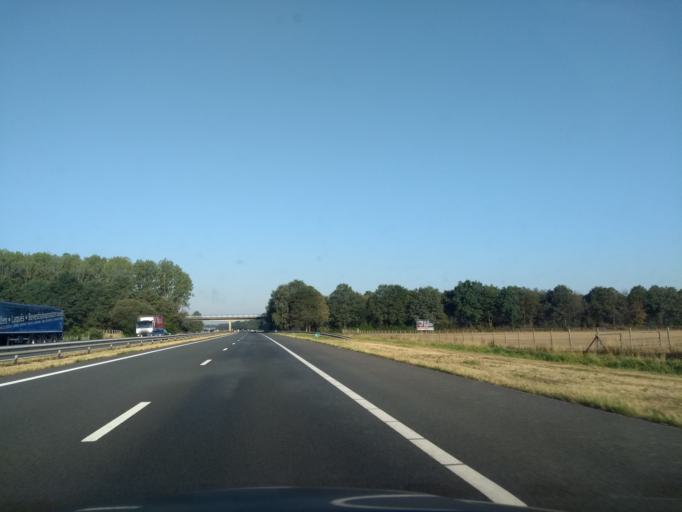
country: NL
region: Gelderland
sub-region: Oude IJsselstreek
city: Wisch
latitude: 51.9445
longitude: 6.4137
